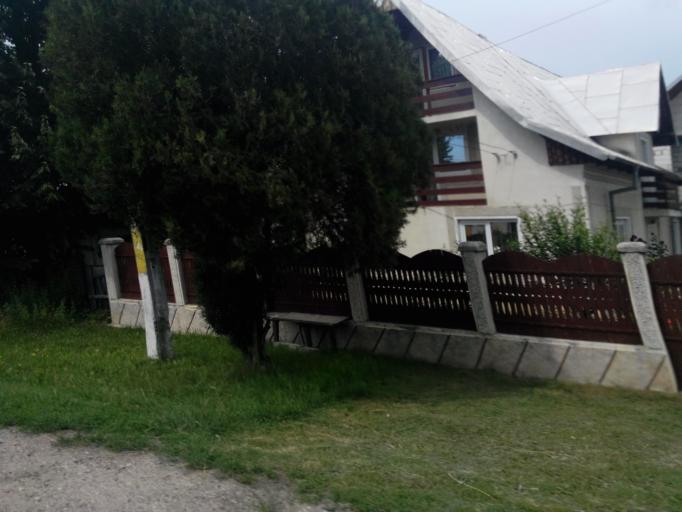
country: RO
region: Arges
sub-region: Comuna Bascov
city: Bascov
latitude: 44.9230
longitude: 24.7946
